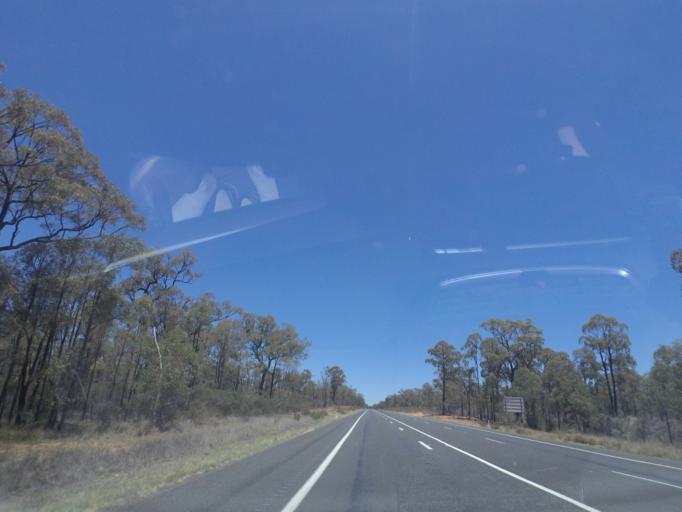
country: AU
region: New South Wales
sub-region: Warrumbungle Shire
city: Coonabarabran
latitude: -30.8704
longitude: 149.4504
